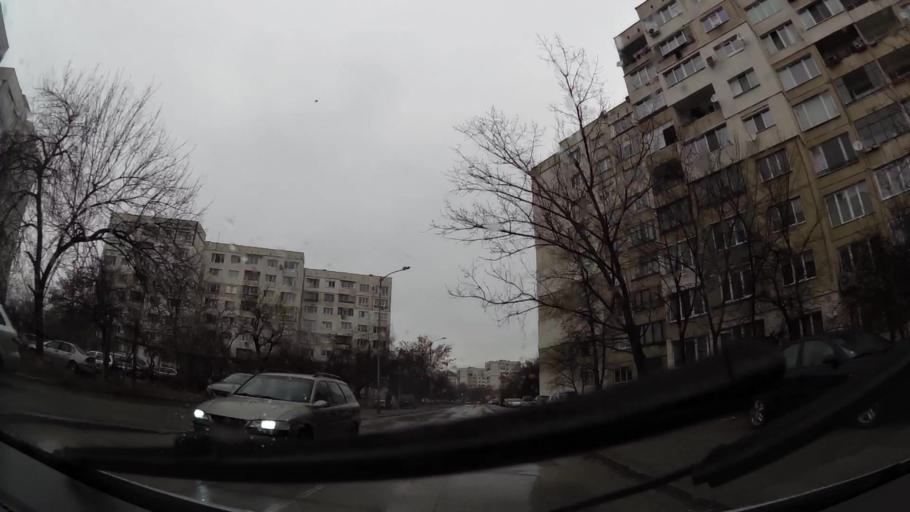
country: BG
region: Sofia-Capital
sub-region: Stolichna Obshtina
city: Sofia
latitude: 42.6368
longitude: 23.3833
